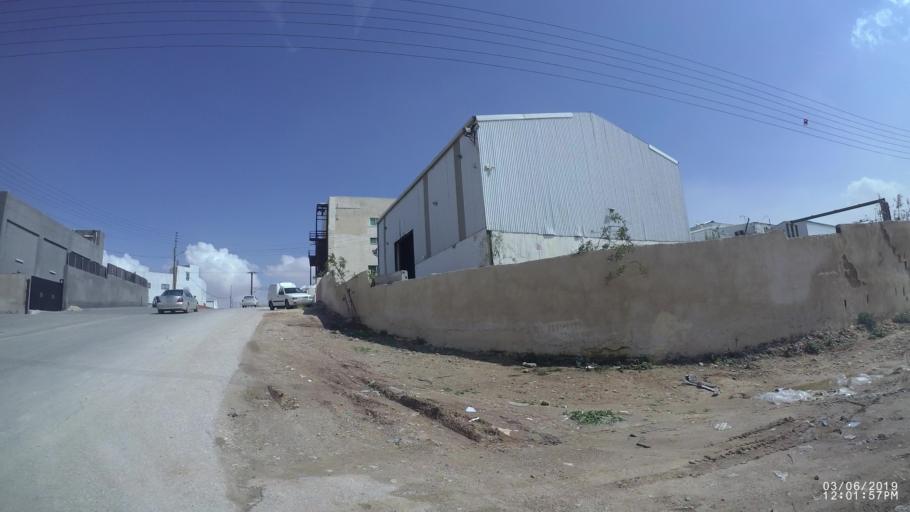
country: JO
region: Zarqa
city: Russeifa
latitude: 31.9877
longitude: 36.0131
